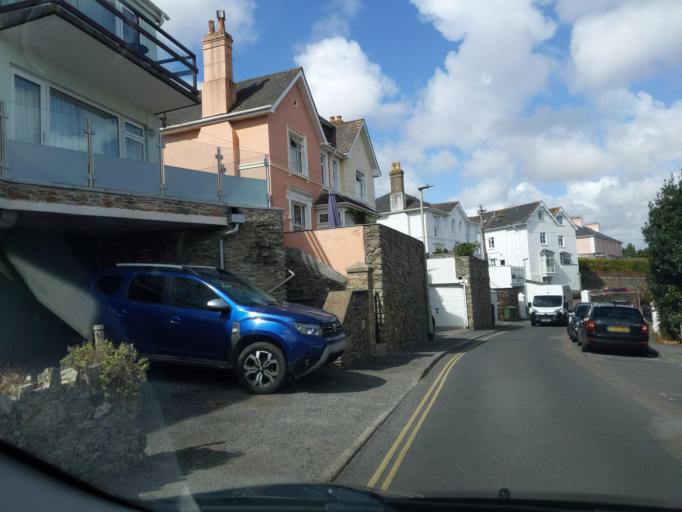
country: GB
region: England
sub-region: Devon
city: Salcombe
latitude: 50.2377
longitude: -3.7696
